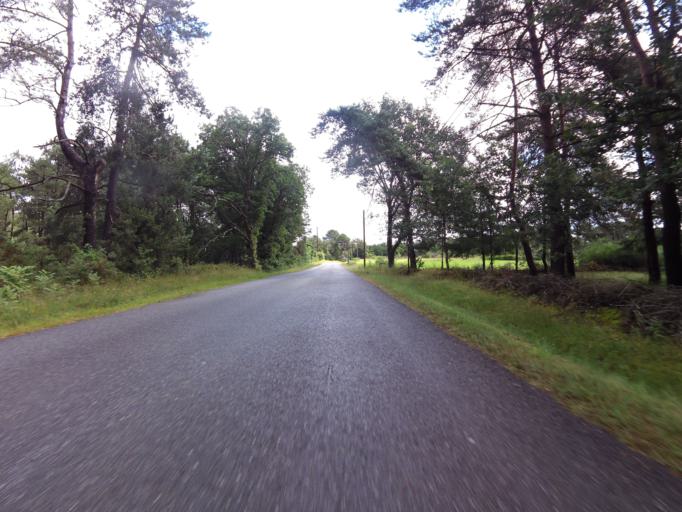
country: FR
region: Brittany
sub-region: Departement du Morbihan
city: Malansac
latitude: 47.7018
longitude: -2.3041
